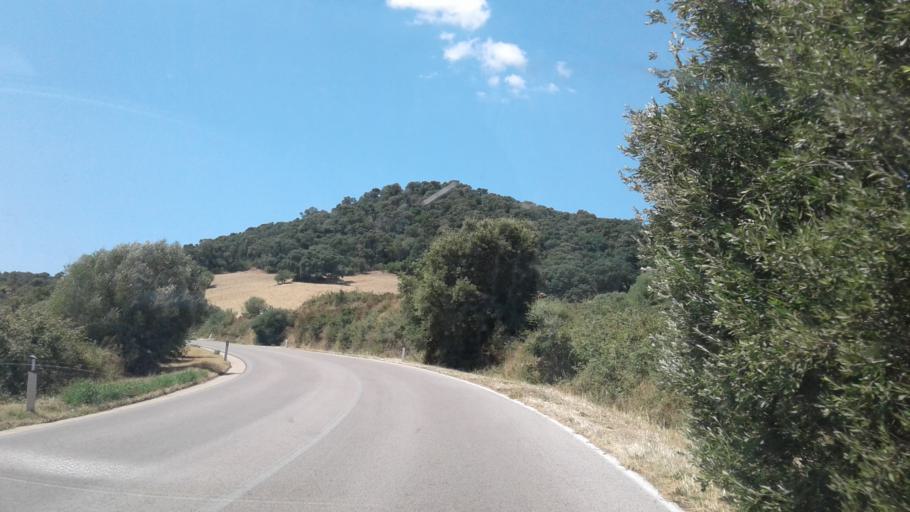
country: IT
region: Sardinia
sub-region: Provincia di Olbia-Tempio
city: Luras
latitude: 40.9539
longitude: 9.2048
